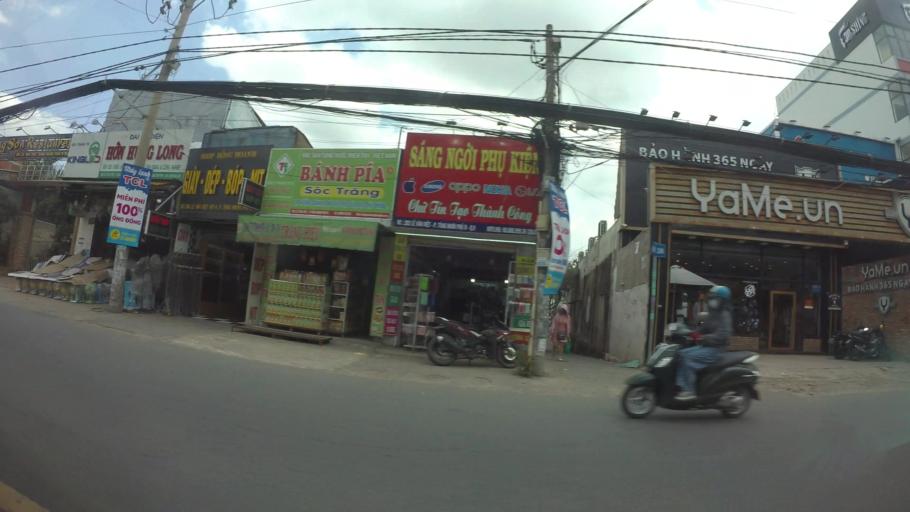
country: VN
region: Ho Chi Minh City
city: Thu Duc
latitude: 10.8442
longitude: 106.7818
